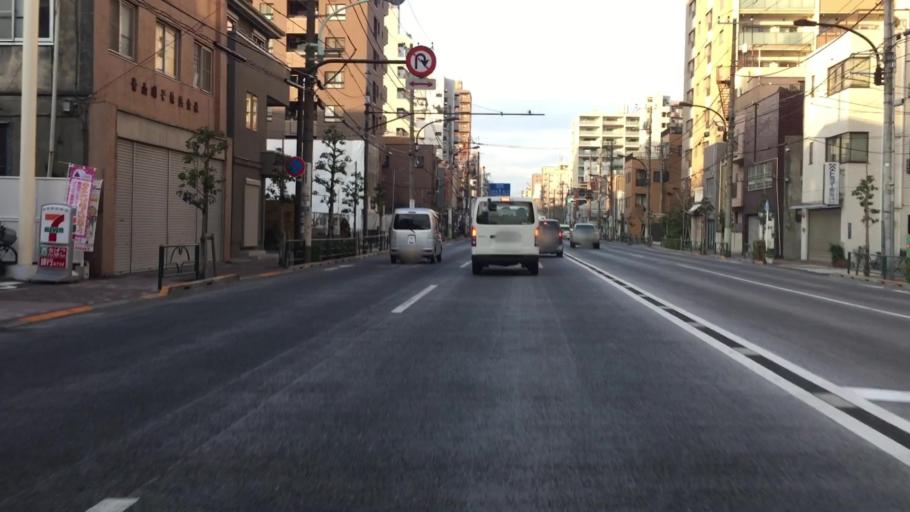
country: JP
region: Tokyo
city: Urayasu
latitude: 35.6935
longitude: 139.8056
